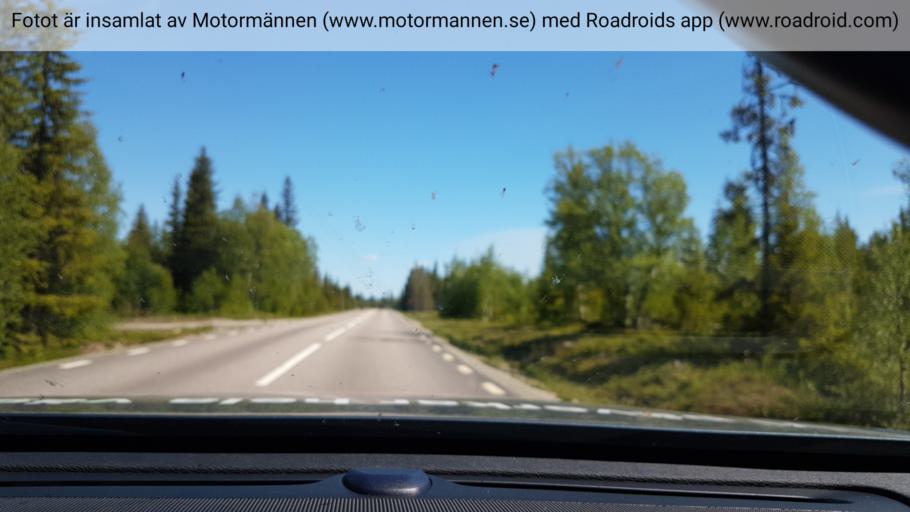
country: SE
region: Vaesterbotten
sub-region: Asele Kommun
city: Insjon
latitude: 64.7300
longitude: 17.5395
